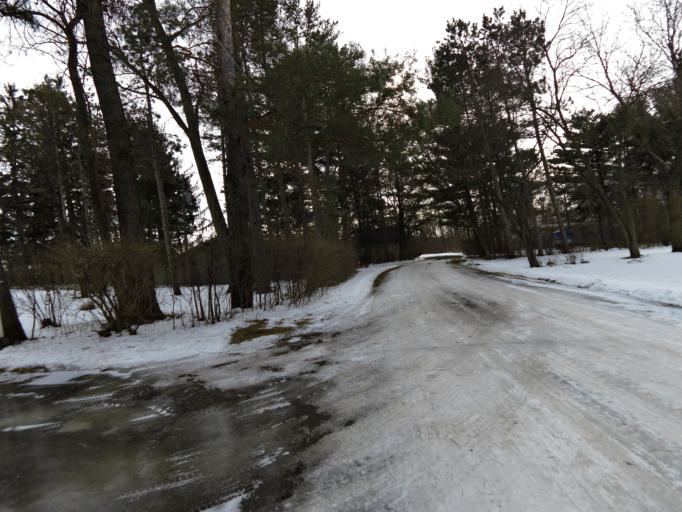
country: US
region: Minnesota
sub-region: Washington County
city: Lake Saint Croix Beach
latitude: 44.9172
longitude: -92.7652
